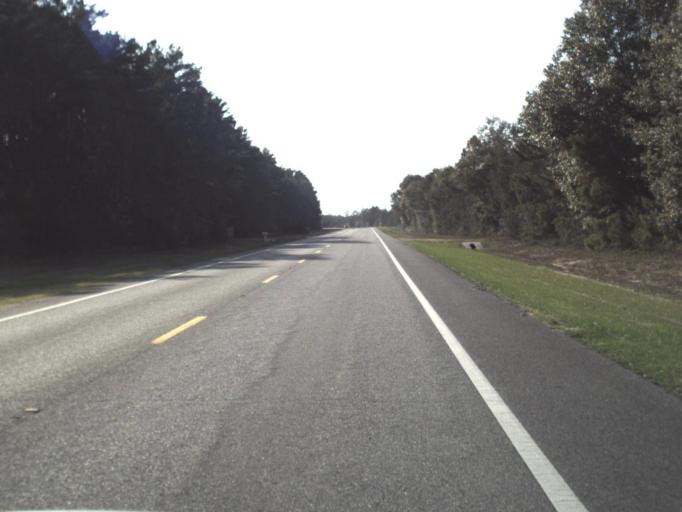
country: US
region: Florida
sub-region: Bay County
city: Youngstown
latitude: 30.4367
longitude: -85.5148
